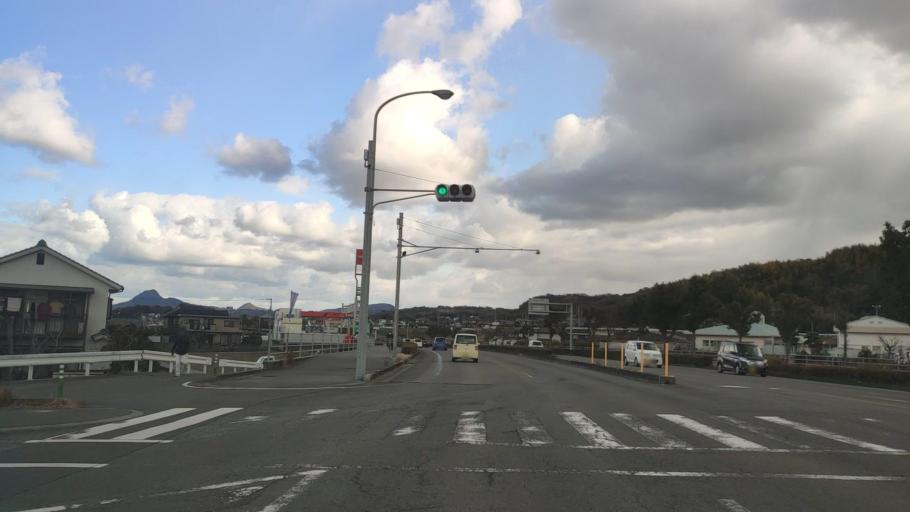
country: JP
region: Ehime
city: Hojo
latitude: 33.9359
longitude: 132.7715
